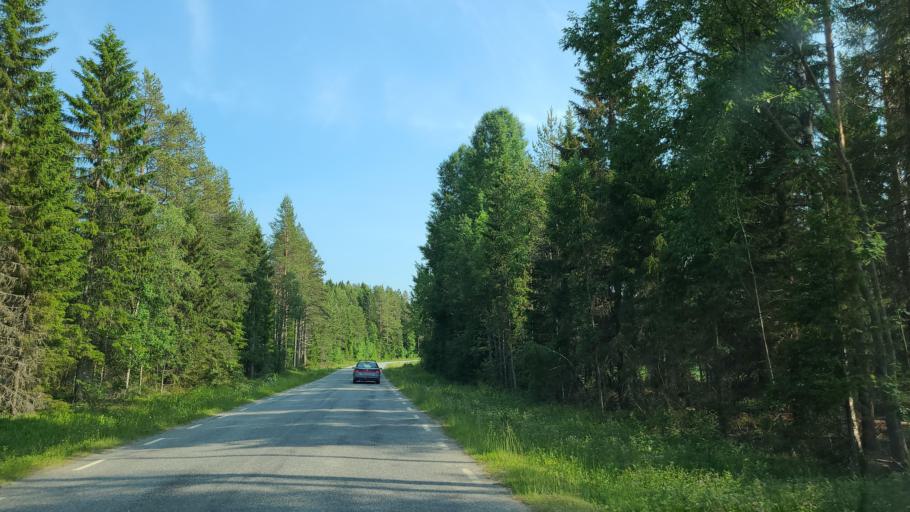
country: SE
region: Vaesterbotten
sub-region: Skelleftea Kommun
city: Burea
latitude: 64.3591
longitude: 21.3362
